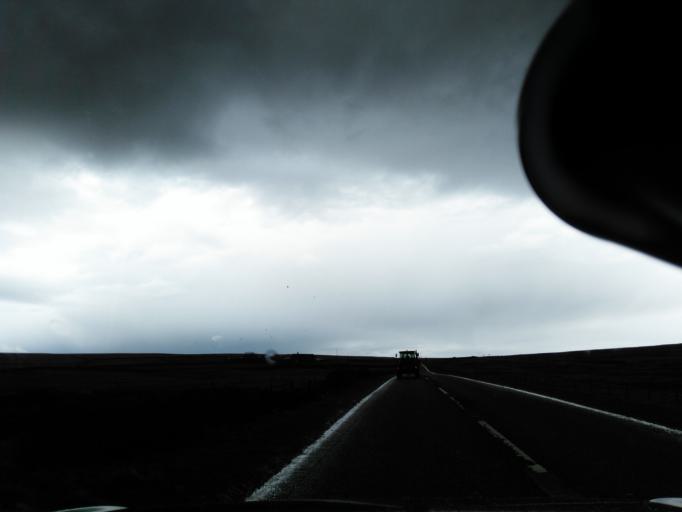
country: GB
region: England
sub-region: Bradford
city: Ilkley
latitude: 53.9892
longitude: -1.8191
